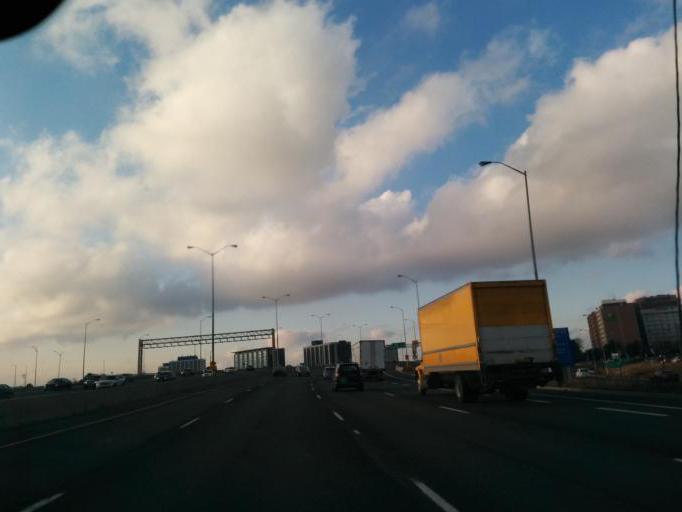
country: CA
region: Ontario
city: Etobicoke
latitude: 43.6839
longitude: -79.5977
